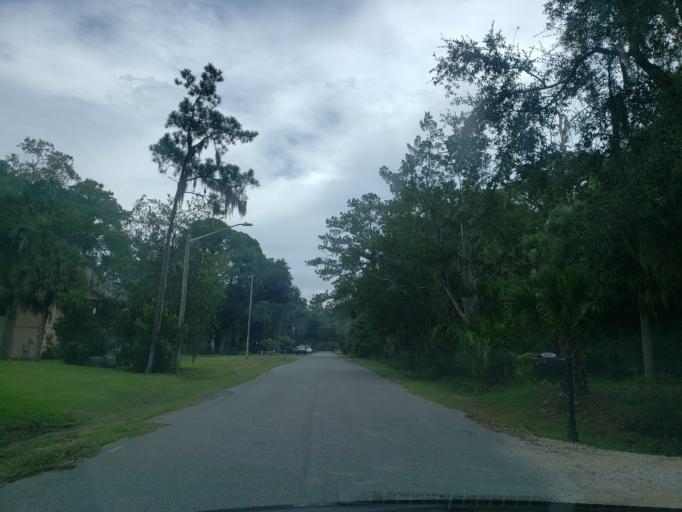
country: US
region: Georgia
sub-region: Chatham County
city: Wilmington Island
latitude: 32.0058
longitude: -80.9596
